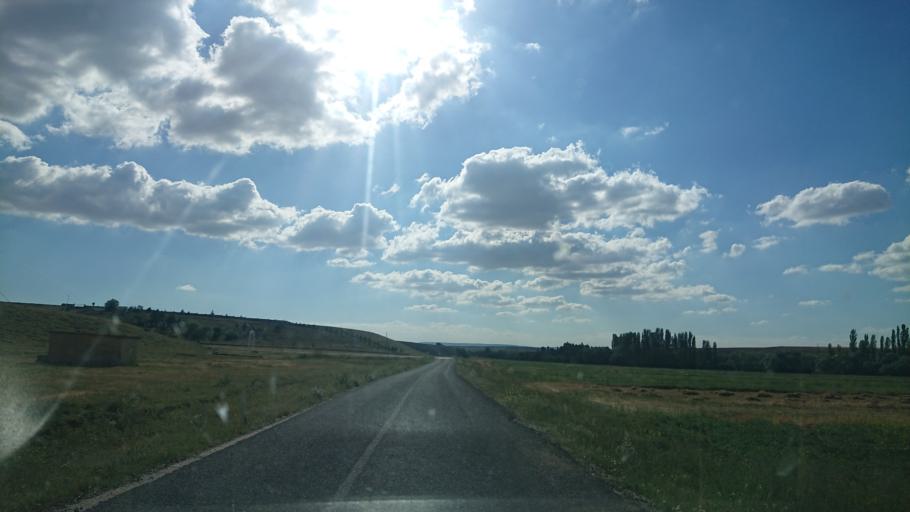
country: TR
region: Aksaray
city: Agacoren
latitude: 38.7561
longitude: 33.9168
